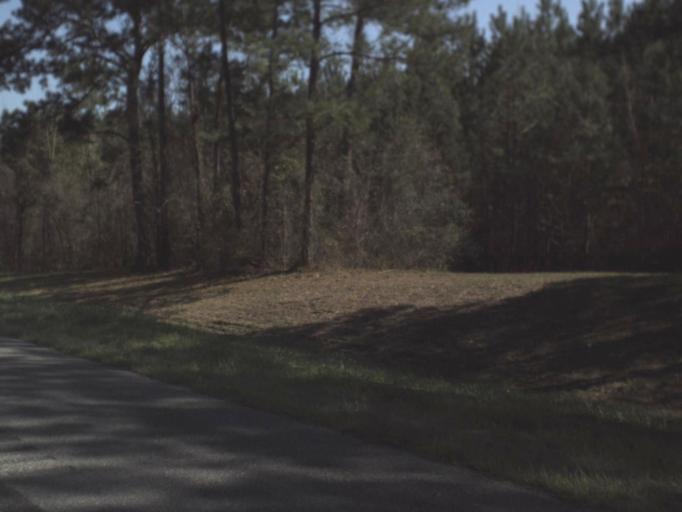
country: US
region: Florida
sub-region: Jackson County
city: Sneads
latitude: 30.6365
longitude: -84.9528
